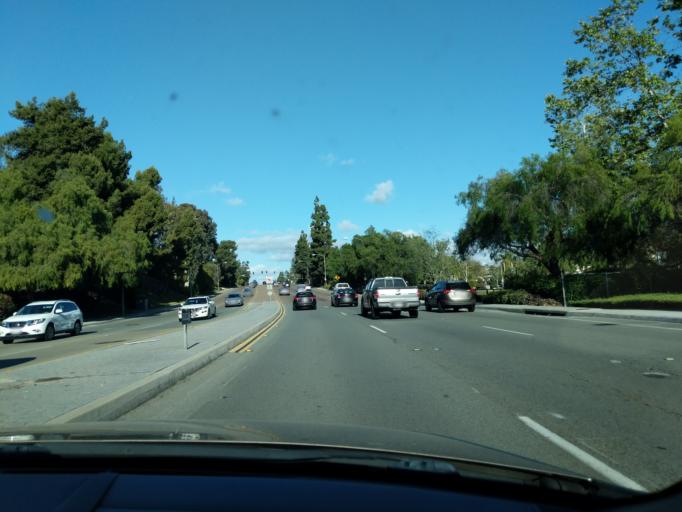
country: US
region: California
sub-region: San Diego County
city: Encinitas
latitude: 33.0670
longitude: -117.2584
